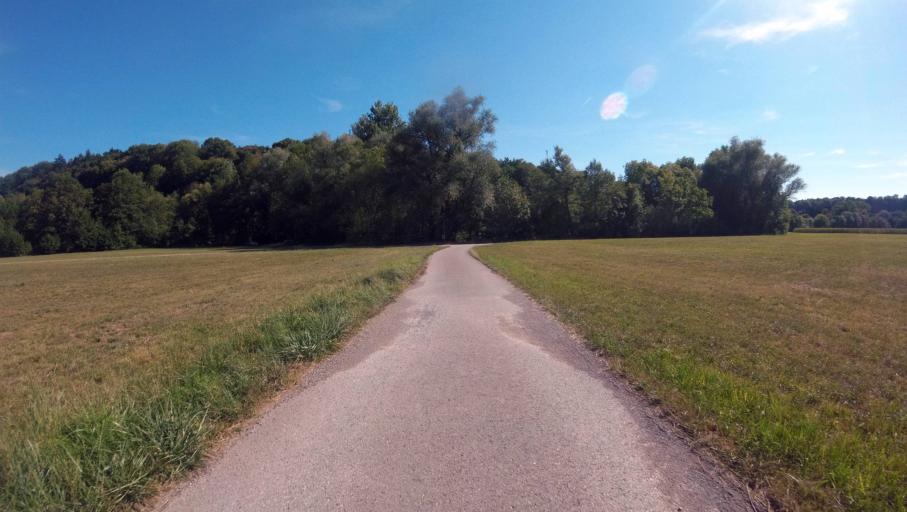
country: DE
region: Baden-Wuerttemberg
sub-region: Regierungsbezirk Stuttgart
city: Burgstetten
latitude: 48.9331
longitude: 9.3747
